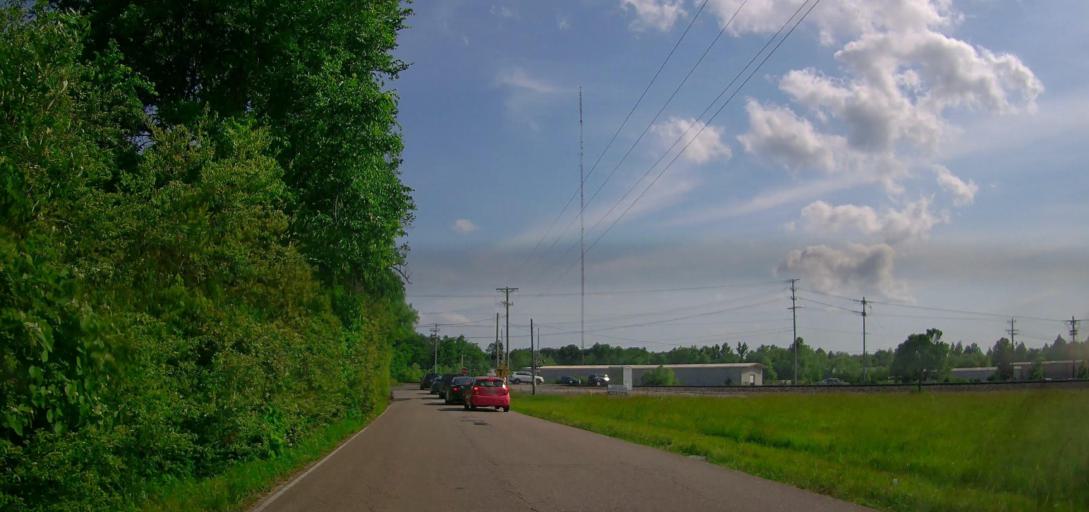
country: US
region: Mississippi
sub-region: De Soto County
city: Olive Branch
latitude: 34.9920
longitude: -89.8619
